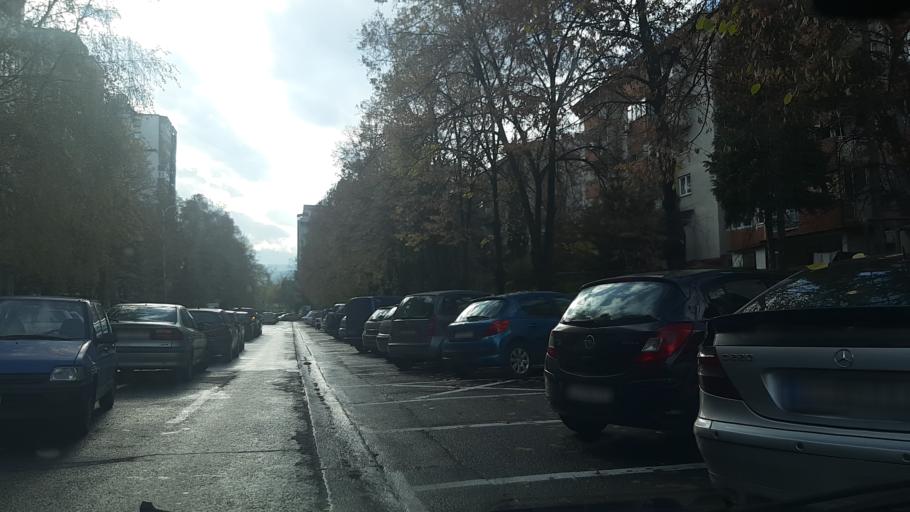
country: MK
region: Kisela Voda
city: Usje
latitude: 41.9848
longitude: 21.4647
